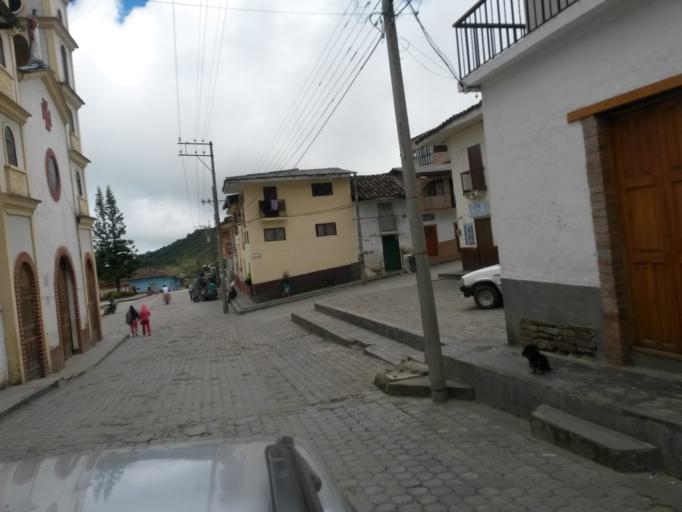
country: CO
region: Cauca
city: Almaguer
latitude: 1.9152
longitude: -76.8540
